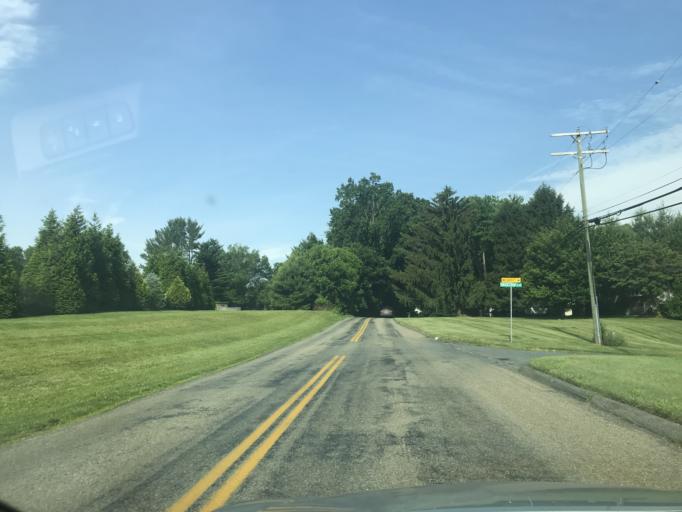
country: US
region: Maryland
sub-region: Harford County
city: Bel Air North
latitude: 39.5563
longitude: -76.4020
